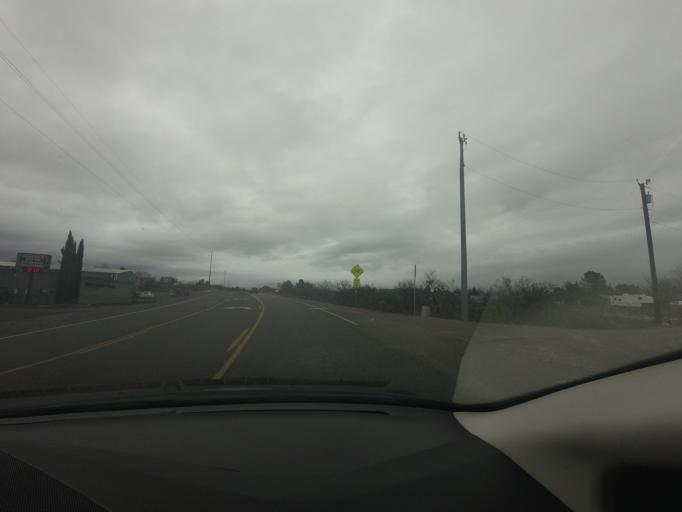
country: US
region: Arizona
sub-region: Yavapai County
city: Lake Montezuma
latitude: 34.6457
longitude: -111.7853
